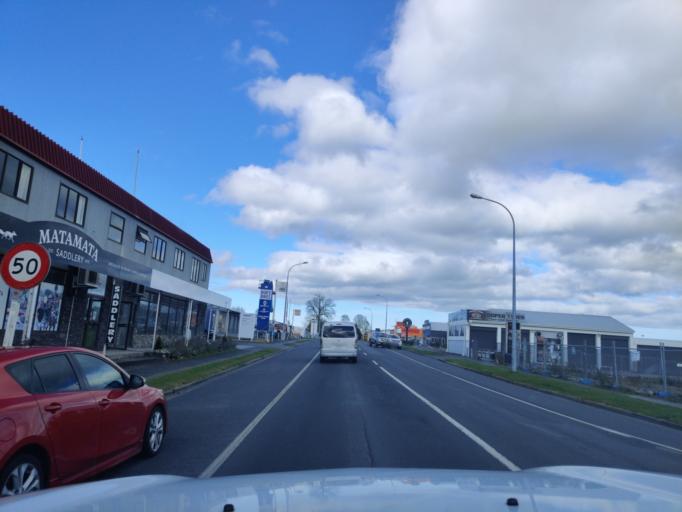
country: NZ
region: Waikato
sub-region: Matamata-Piako District
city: Matamata
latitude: -37.8100
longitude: 175.7706
